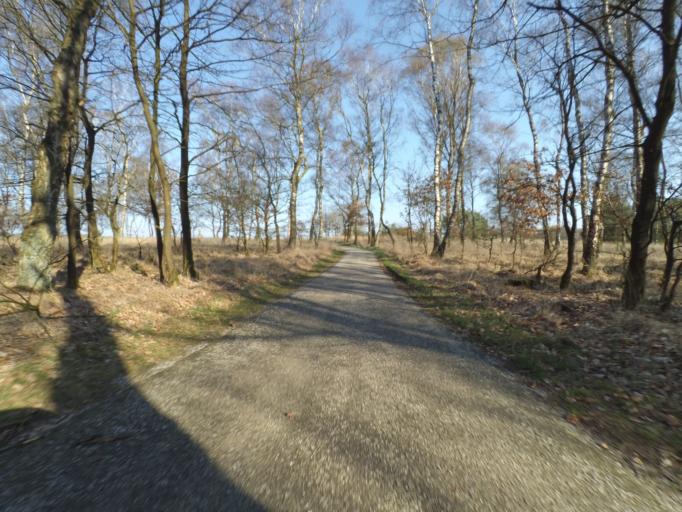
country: NL
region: Gelderland
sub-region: Gemeente Arnhem
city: Hoogkamp
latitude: 52.0610
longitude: 5.8509
